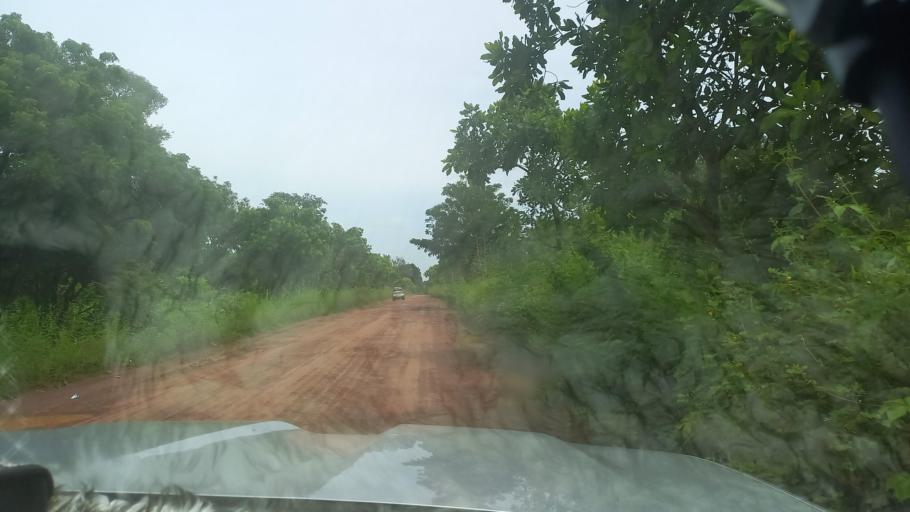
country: SN
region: Kolda
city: Marsassoum
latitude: 12.9028
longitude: -16.0231
